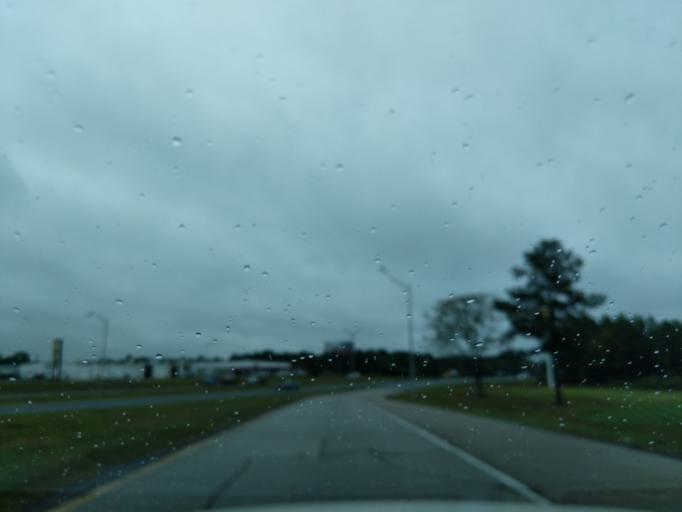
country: US
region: Louisiana
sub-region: Caddo Parish
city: Greenwood
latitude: 32.4466
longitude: -93.8988
